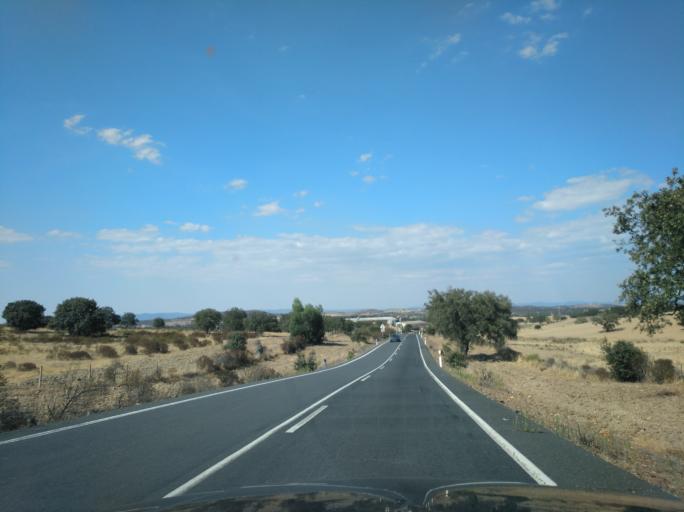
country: ES
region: Andalusia
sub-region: Provincia de Huelva
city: Alosno
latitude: 37.6402
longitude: -7.1292
